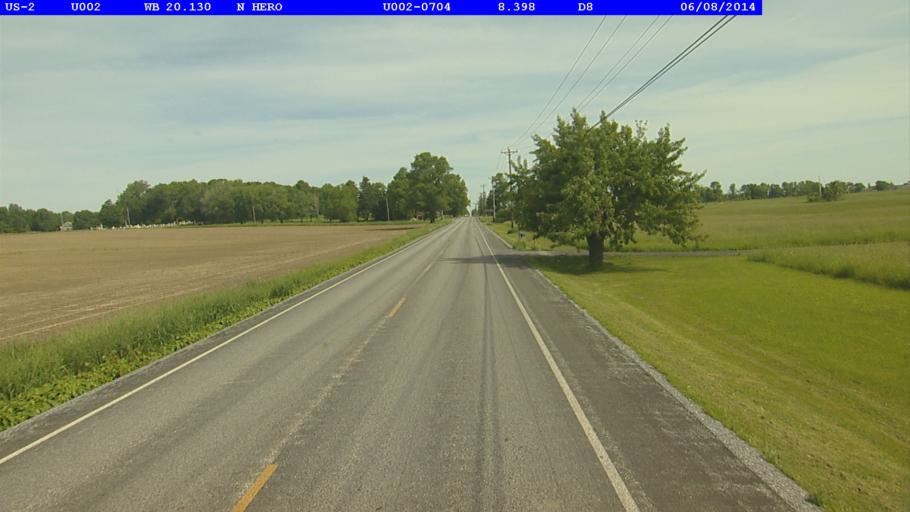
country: US
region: Vermont
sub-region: Grand Isle County
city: North Hero
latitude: 44.7789
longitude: -73.2936
